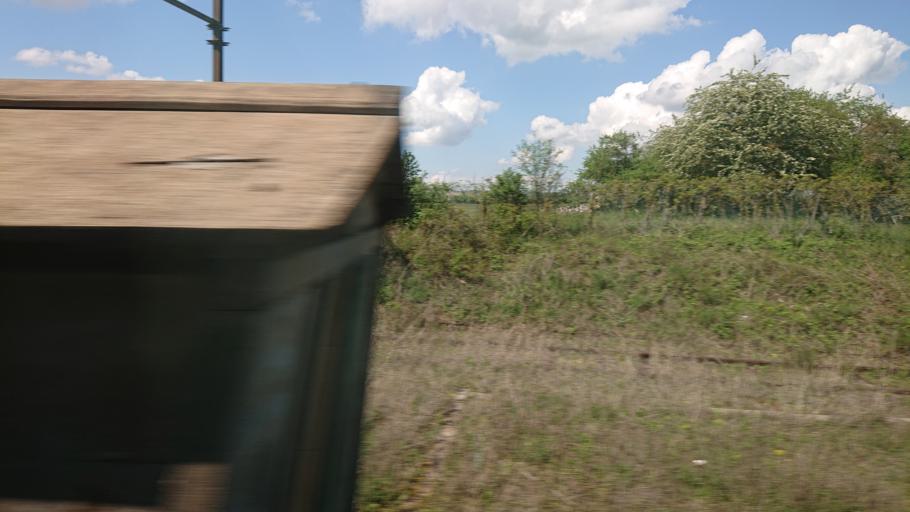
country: FR
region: Rhone-Alpes
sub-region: Departement de l'Ain
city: Leyment
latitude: 45.9305
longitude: 5.2690
